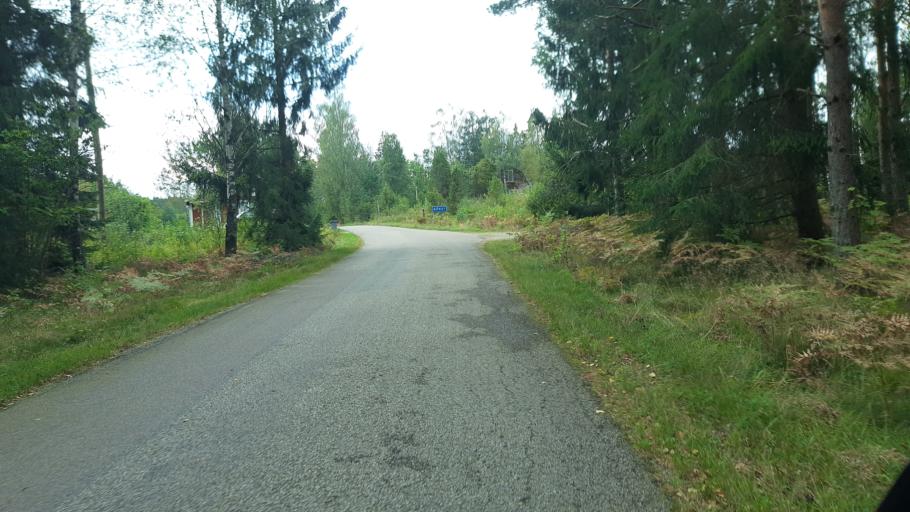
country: SE
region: Kronoberg
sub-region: Tingsryds Kommun
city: Tingsryd
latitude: 56.4729
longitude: 15.1567
